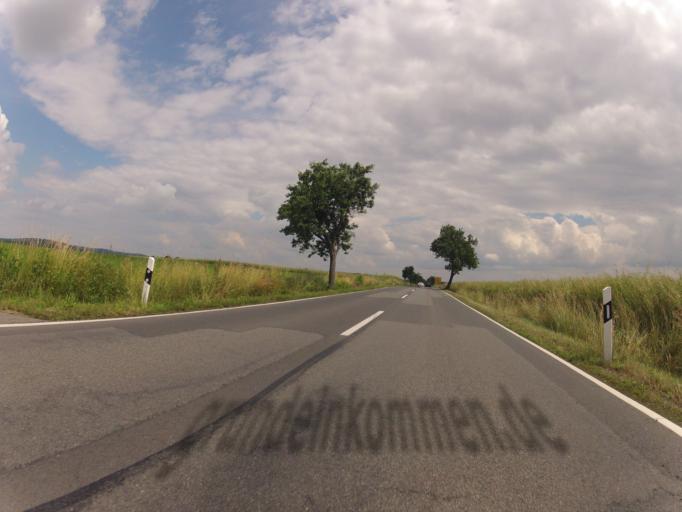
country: DE
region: Saxony
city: Hohburg
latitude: 51.3838
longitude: 12.7969
